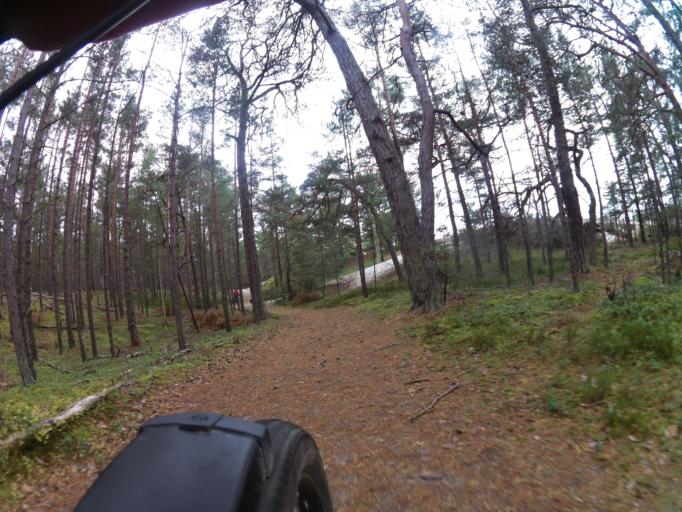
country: PL
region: Pomeranian Voivodeship
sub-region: Powiat pucki
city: Hel
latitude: 54.6264
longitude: 18.8030
